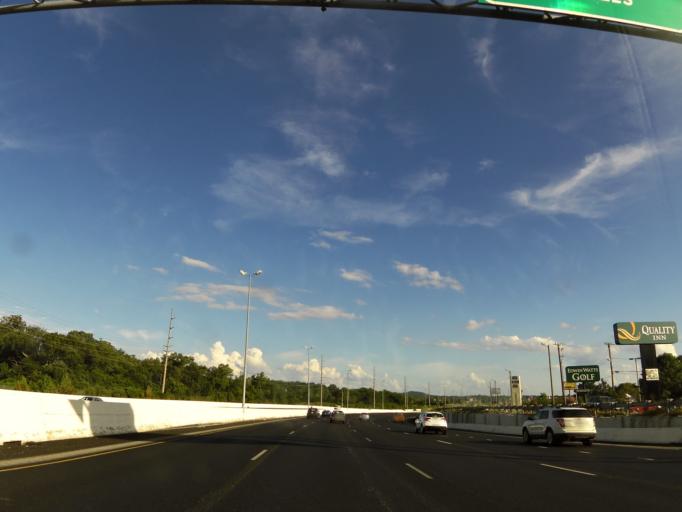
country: US
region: Tennessee
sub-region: Davidson County
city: Lakewood
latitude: 36.2257
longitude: -86.6954
